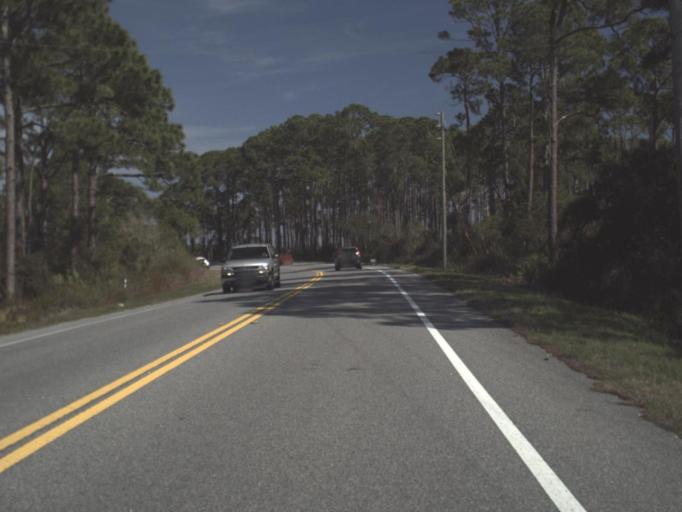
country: US
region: Florida
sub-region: Franklin County
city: Carrabelle
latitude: 29.7931
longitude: -84.7537
